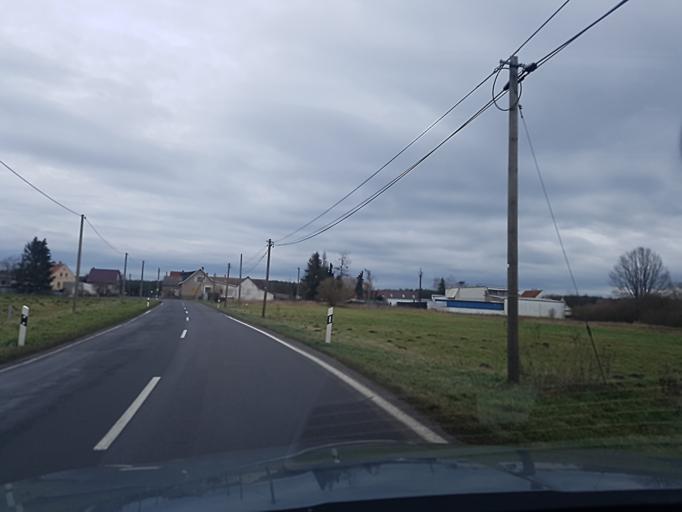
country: DE
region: Brandenburg
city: Schilda
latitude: 51.6151
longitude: 13.3602
